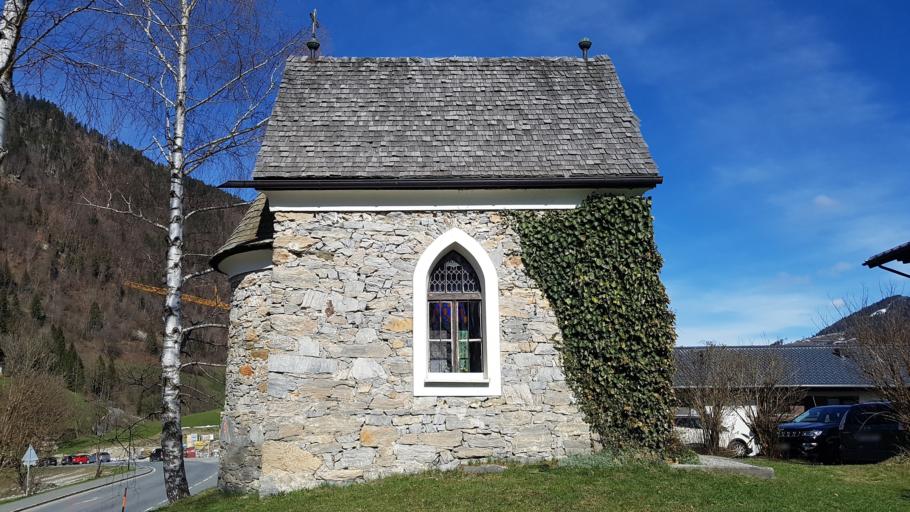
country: AT
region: Salzburg
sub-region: Politischer Bezirk Sankt Johann im Pongau
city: Sankt Veit im Pongau
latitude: 47.3282
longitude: 13.1599
